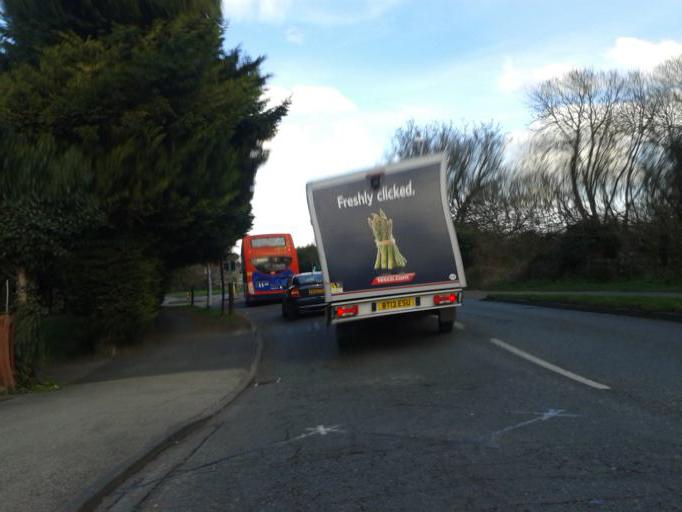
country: GB
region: England
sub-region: Cambridgeshire
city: Fulbourn
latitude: 52.1834
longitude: 0.1708
